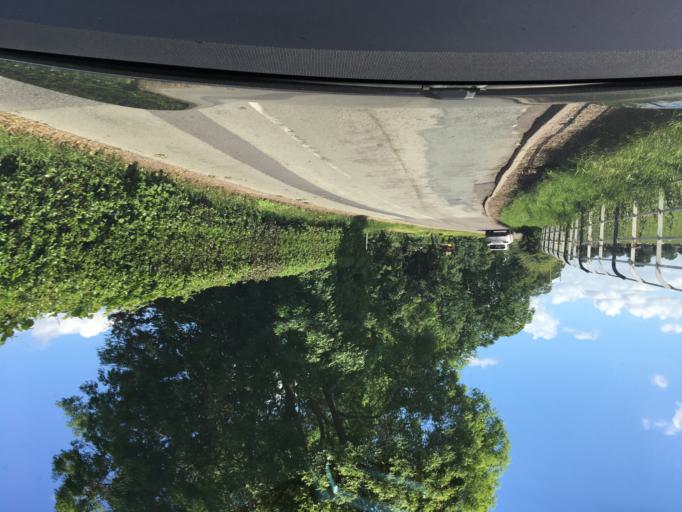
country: GB
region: England
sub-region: Cheshire East
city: Mobberley
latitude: 53.3011
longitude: -2.2973
